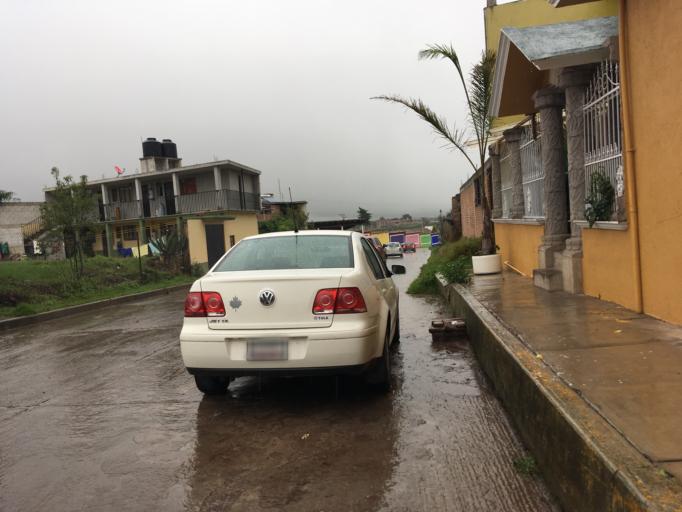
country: MX
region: Puebla
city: Chignahuapan
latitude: 19.8394
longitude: -98.0259
